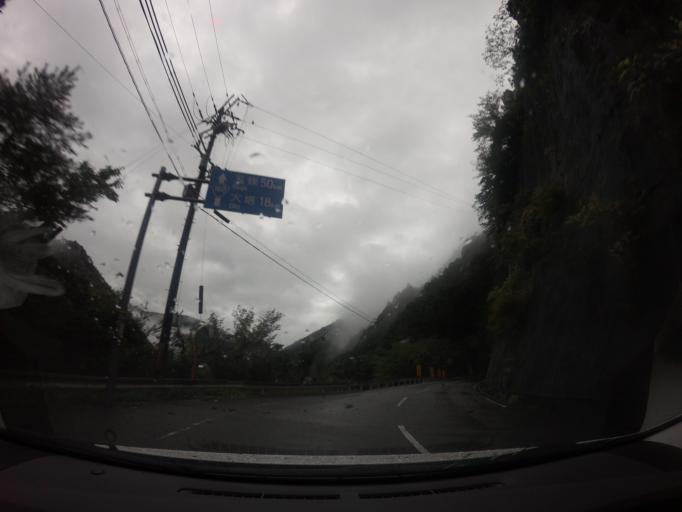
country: JP
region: Wakayama
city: Koya
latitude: 34.0613
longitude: 135.7448
